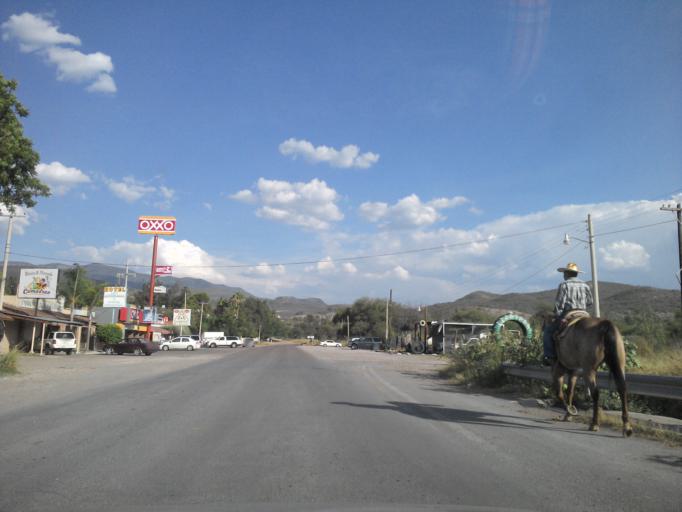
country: MX
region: Zacatecas
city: Juchipila
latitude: 21.2612
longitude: -103.1592
